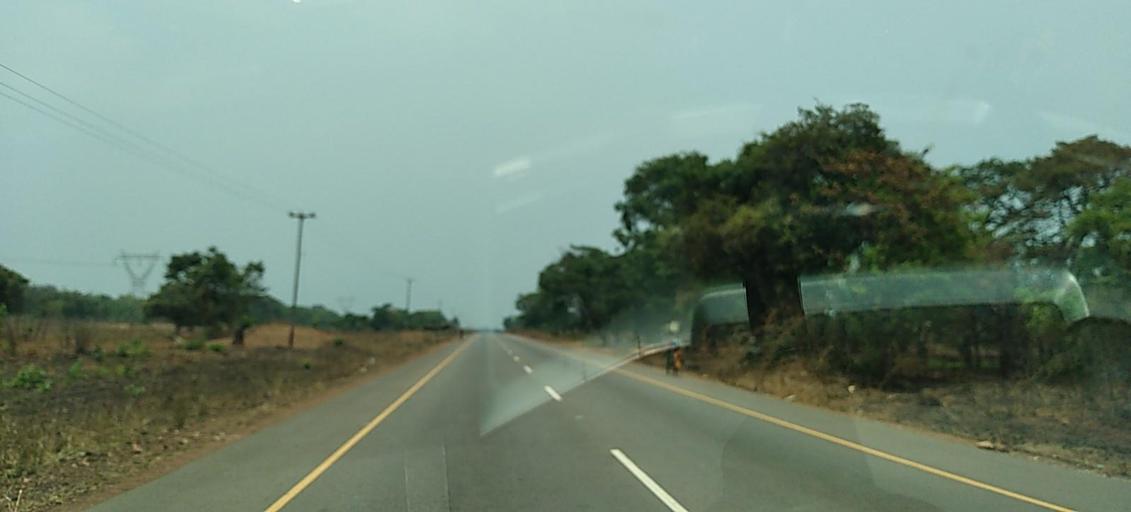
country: ZM
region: Copperbelt
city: Chililabombwe
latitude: -12.4035
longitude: 27.3798
